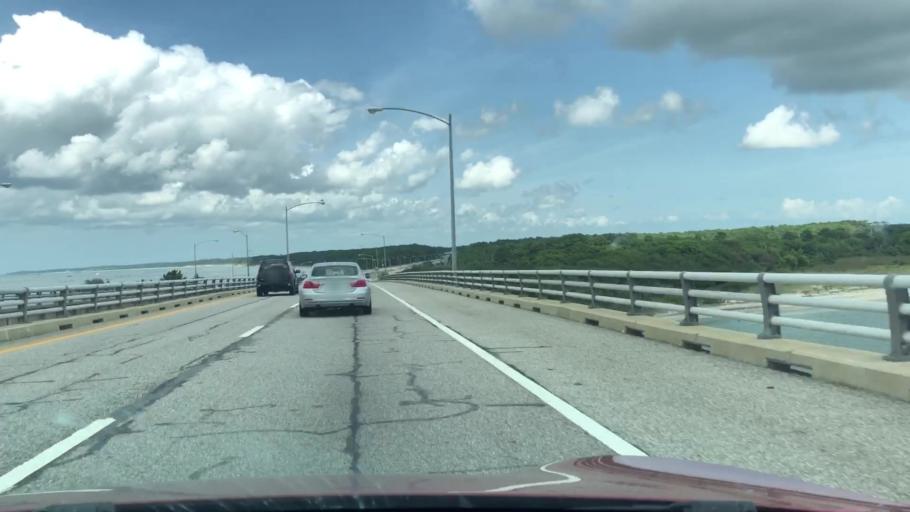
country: US
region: Virginia
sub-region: Northampton County
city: Cape Charles
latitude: 37.1161
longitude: -75.9691
